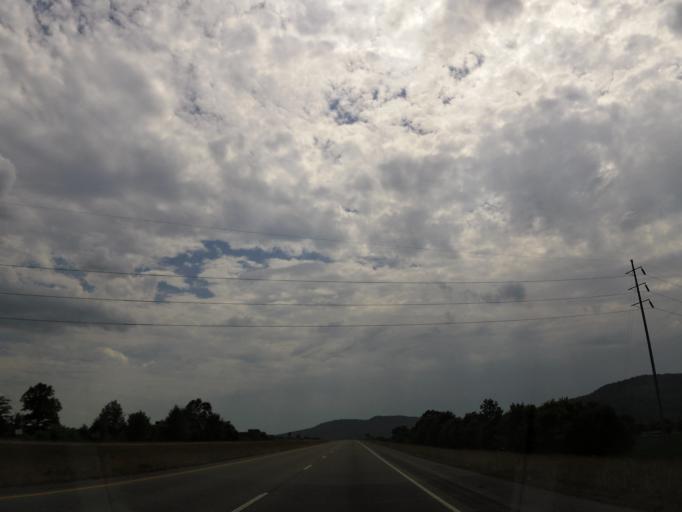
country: US
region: Tennessee
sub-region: Marion County
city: South Pittsburg
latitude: 34.9883
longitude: -85.7174
